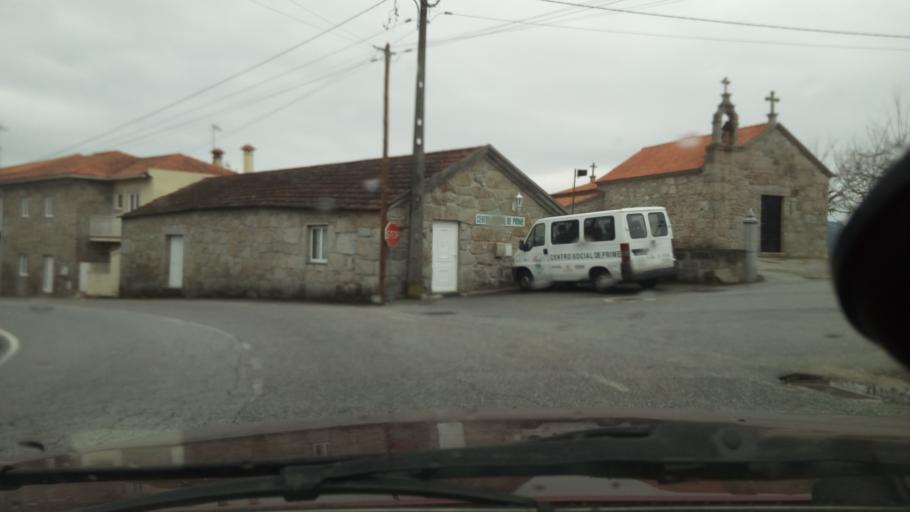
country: PT
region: Viseu
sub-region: Viseu
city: Rio de Loba
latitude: 40.6384
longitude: -7.8396
